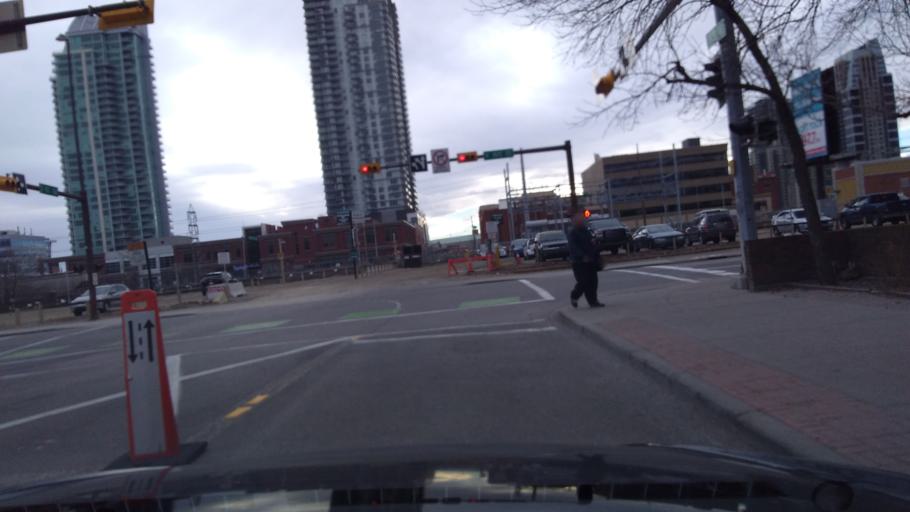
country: CA
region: Alberta
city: Calgary
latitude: 51.0446
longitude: -114.0557
